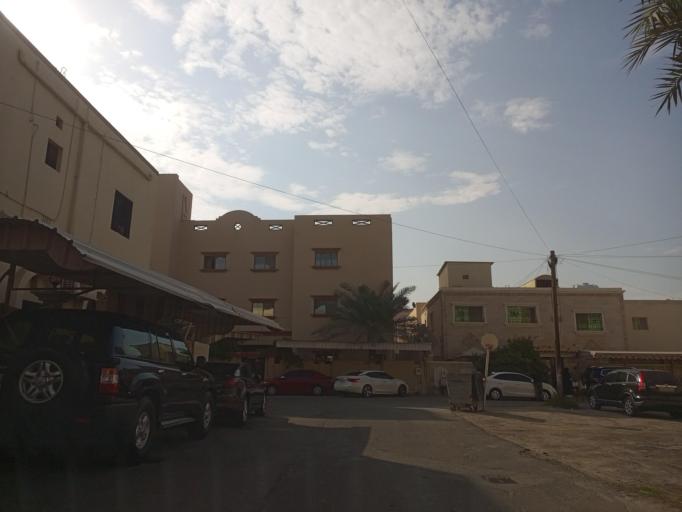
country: BH
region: Muharraq
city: Al Hadd
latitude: 26.2488
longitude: 50.6438
